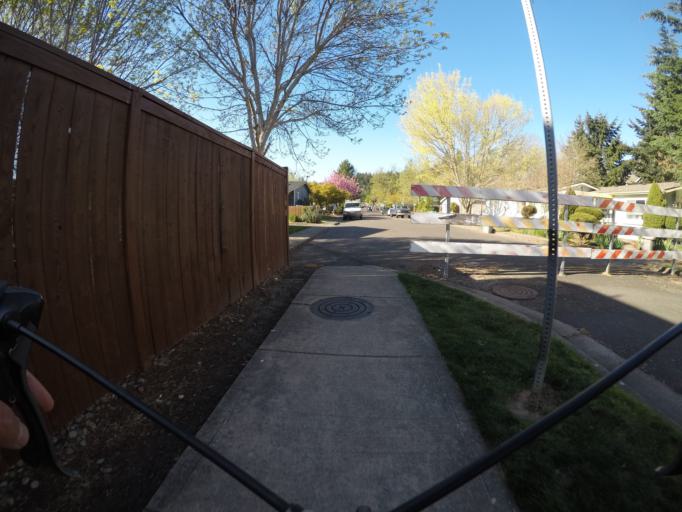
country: US
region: Oregon
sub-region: Washington County
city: King City
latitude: 45.3996
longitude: -122.8157
